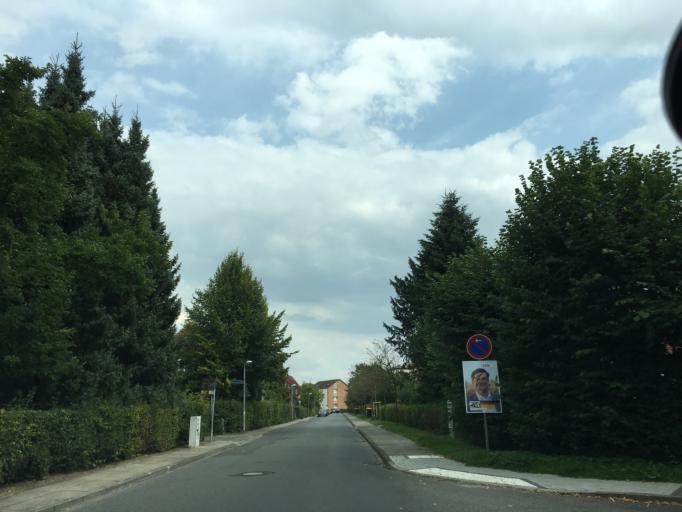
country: DE
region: Lower Saxony
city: Lueneburg
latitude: 53.2572
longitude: 10.3832
